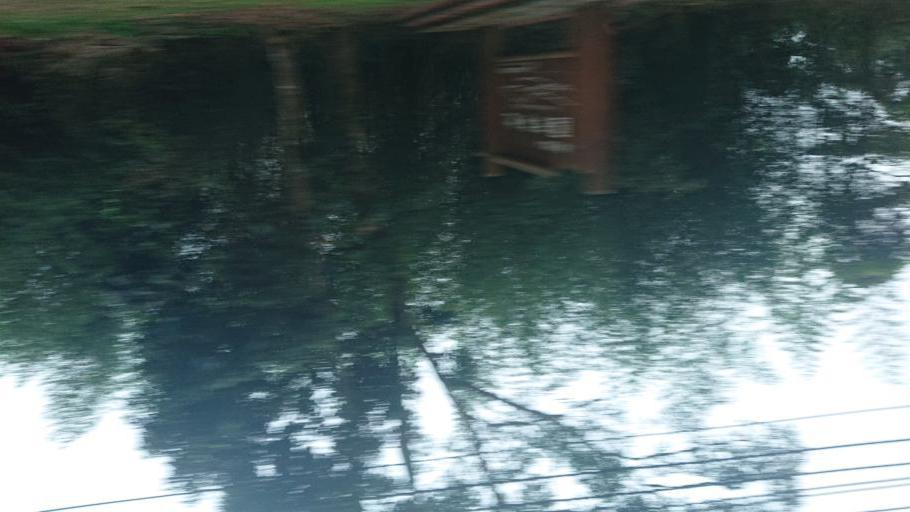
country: TW
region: Taiwan
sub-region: Chiayi
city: Jiayi Shi
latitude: 23.4757
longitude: 120.7194
